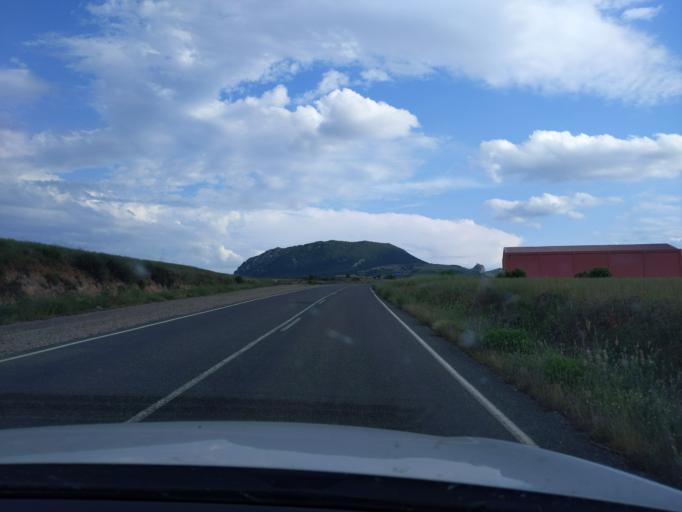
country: ES
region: La Rioja
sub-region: Provincia de La Rioja
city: Alberite
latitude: 42.3820
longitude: -2.4242
